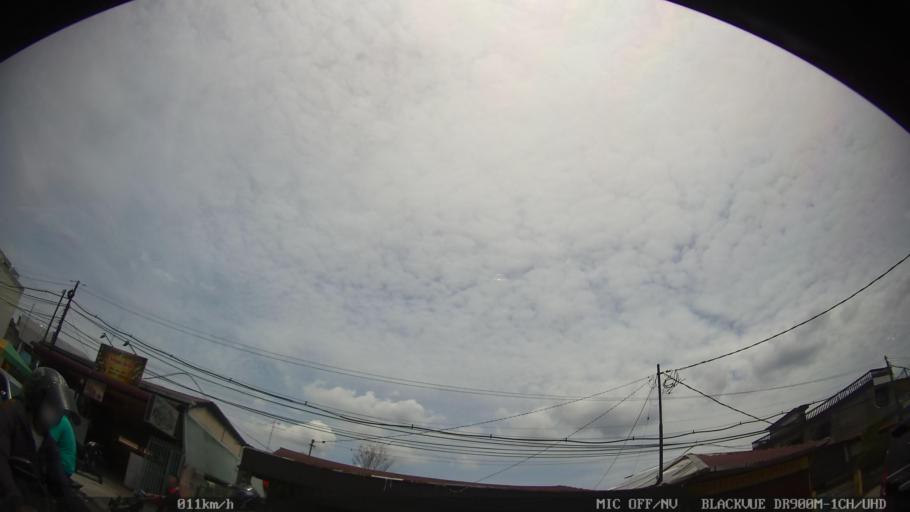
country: ID
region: North Sumatra
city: Deli Tua
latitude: 3.5299
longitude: 98.6394
